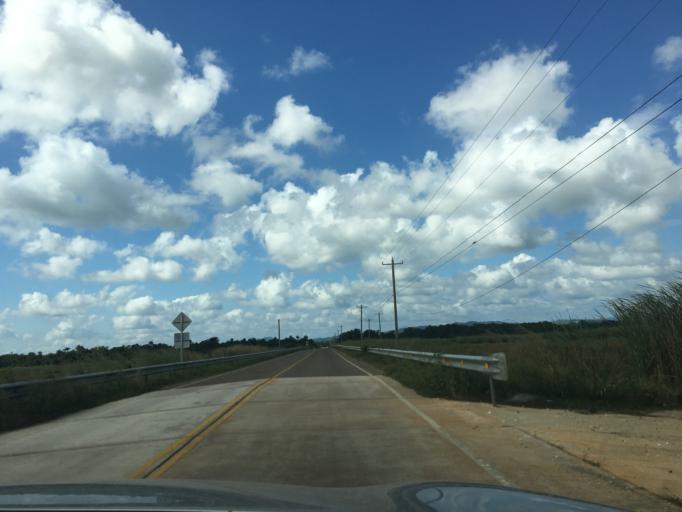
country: BZ
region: Stann Creek
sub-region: Dangriga
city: Dangriga
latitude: 16.8594
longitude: -88.2984
